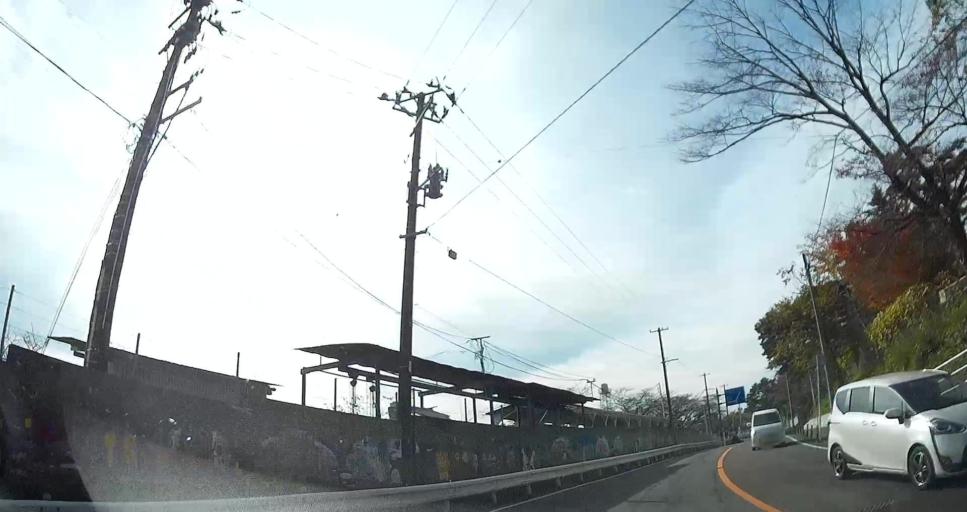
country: JP
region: Miyagi
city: Sendai
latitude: 38.2468
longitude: 140.8480
